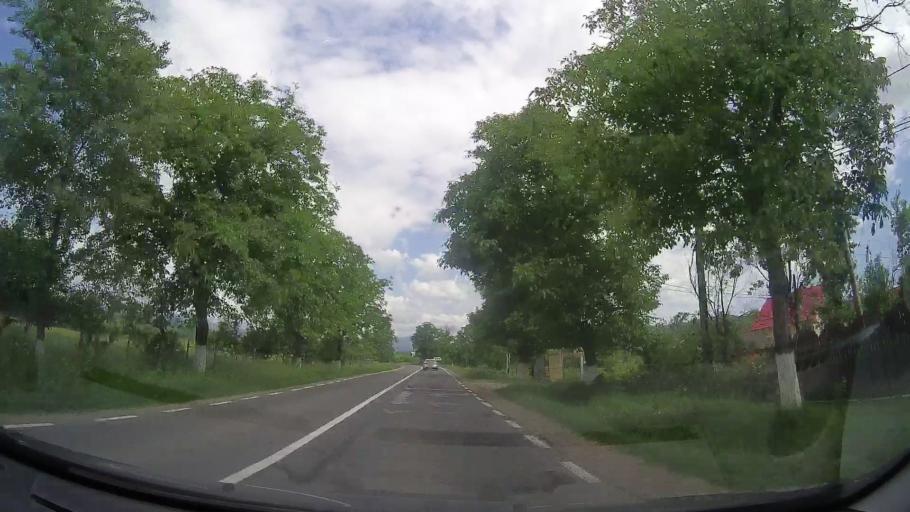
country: RO
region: Prahova
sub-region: Comuna Izvoarele
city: Homoraciu
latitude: 45.2408
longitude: 26.0279
